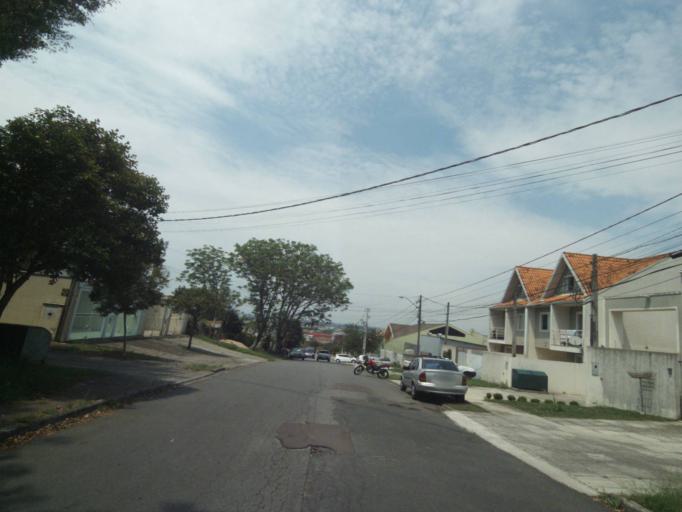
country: BR
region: Parana
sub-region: Pinhais
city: Pinhais
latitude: -25.4257
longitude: -49.2066
